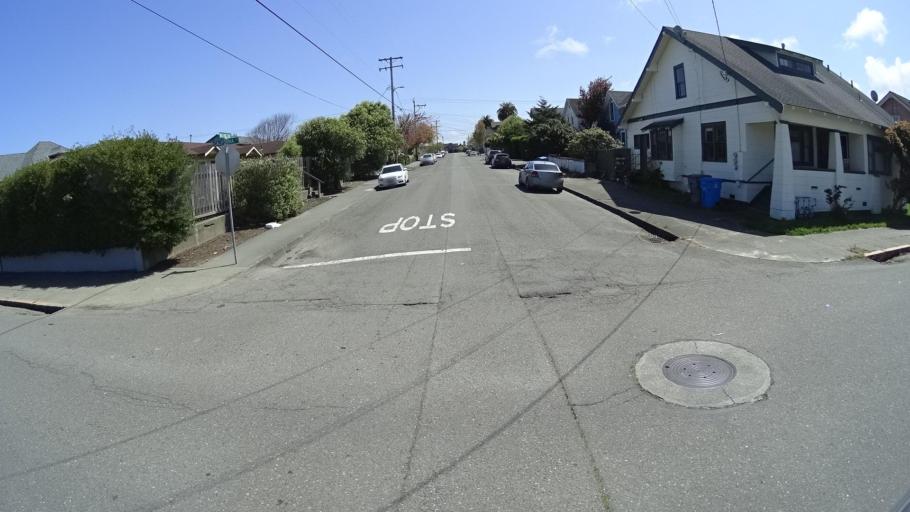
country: US
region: California
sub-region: Humboldt County
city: Eureka
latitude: 40.7983
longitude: -124.1719
